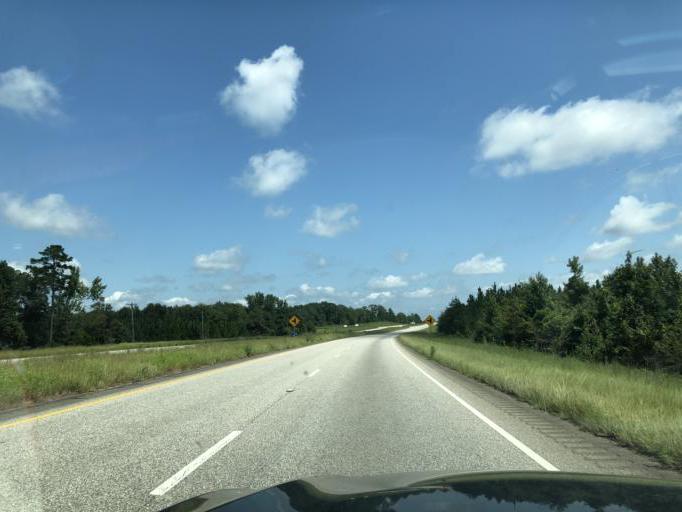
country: US
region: Alabama
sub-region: Henry County
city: Abbeville
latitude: 31.7176
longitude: -85.2702
